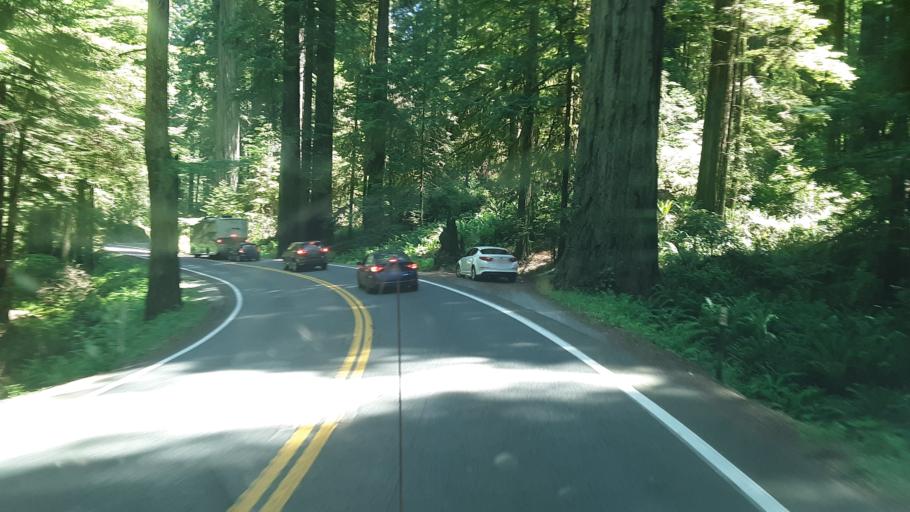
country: US
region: California
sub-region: Del Norte County
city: Bertsch-Oceanview
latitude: 41.8113
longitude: -124.1172
